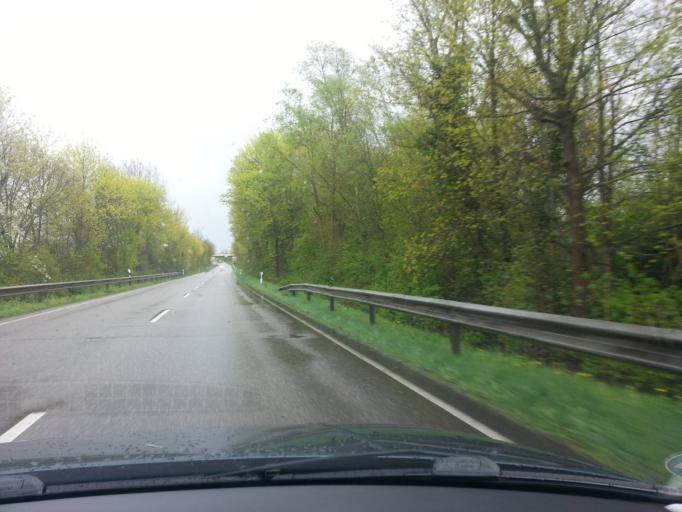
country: DE
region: Rheinland-Pfalz
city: Offenbach an der Queich
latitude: 49.2027
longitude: 8.1940
